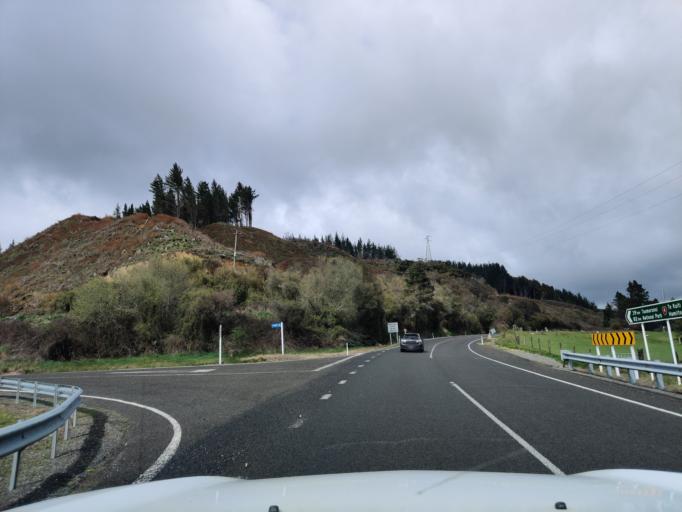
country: NZ
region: Waikato
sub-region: Otorohanga District
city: Otorohanga
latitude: -38.6156
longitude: 175.2193
